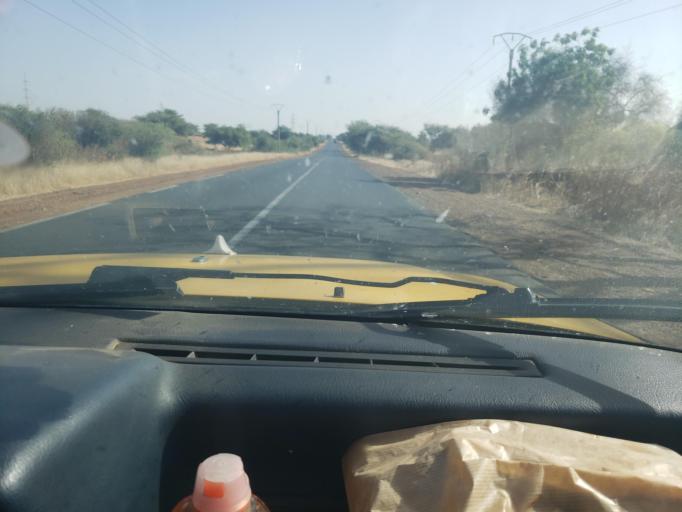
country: SN
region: Louga
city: Louga
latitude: 15.6611
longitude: -16.2579
